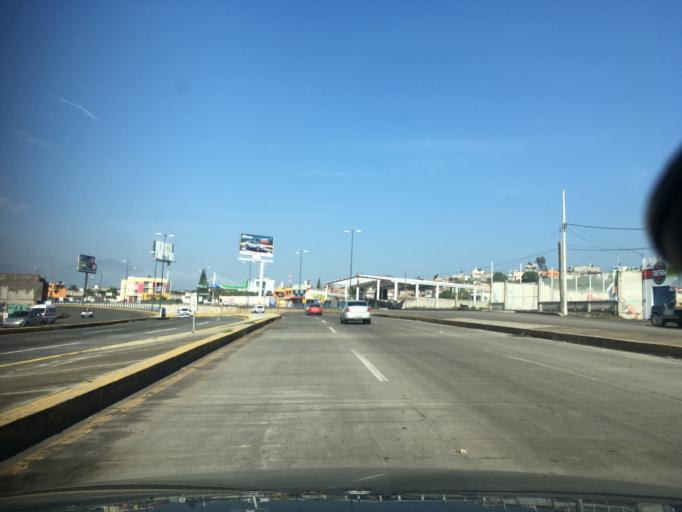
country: MX
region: Michoacan
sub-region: Morelia
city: San Antonio
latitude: 19.7056
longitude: -101.2426
